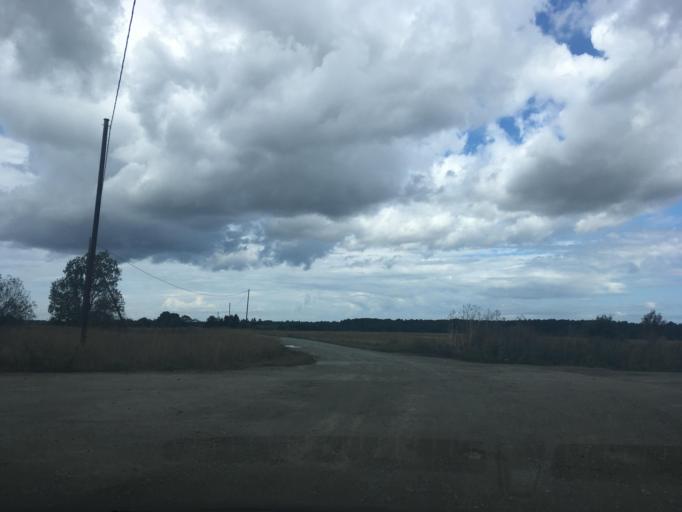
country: EE
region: Harju
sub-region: Rae vald
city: Jueri
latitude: 59.3812
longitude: 24.8876
